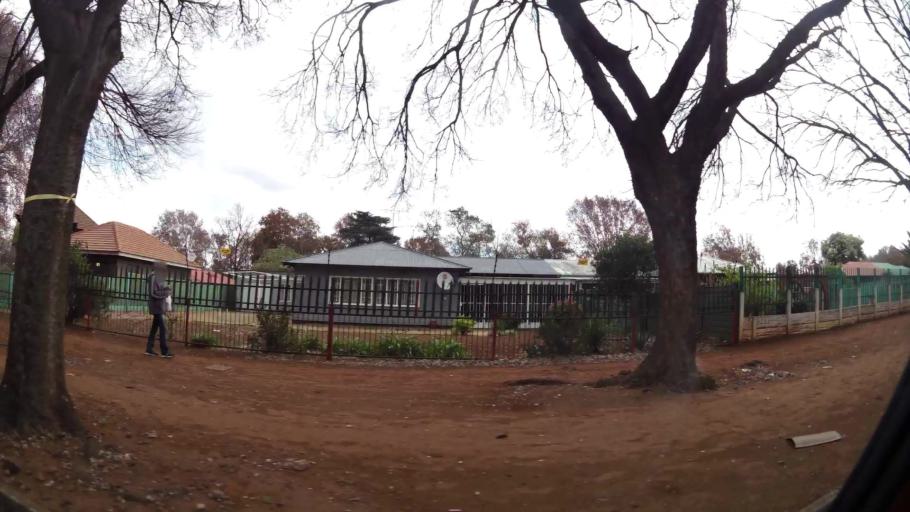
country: ZA
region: Gauteng
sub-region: Sedibeng District Municipality
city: Vanderbijlpark
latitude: -26.7049
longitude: 27.8239
